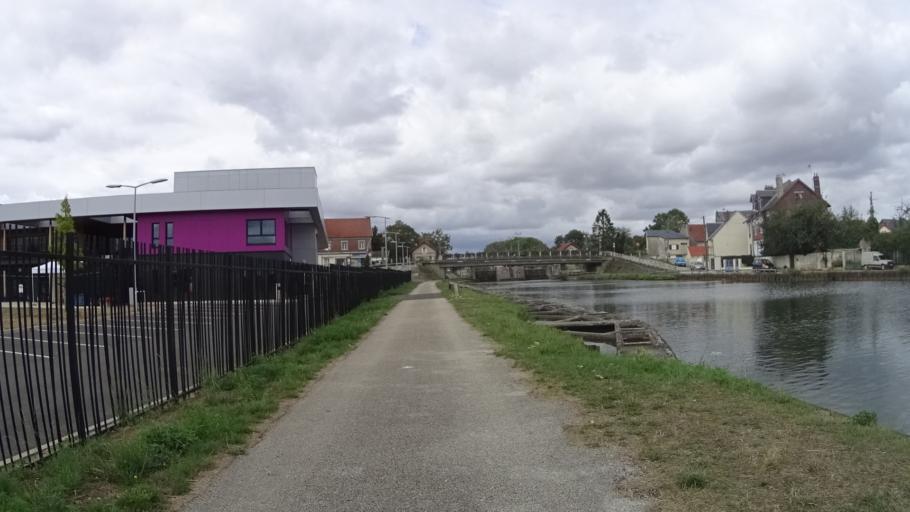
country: FR
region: Picardie
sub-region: Departement de l'Aisne
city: Tergnier
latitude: 49.6554
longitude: 3.3026
